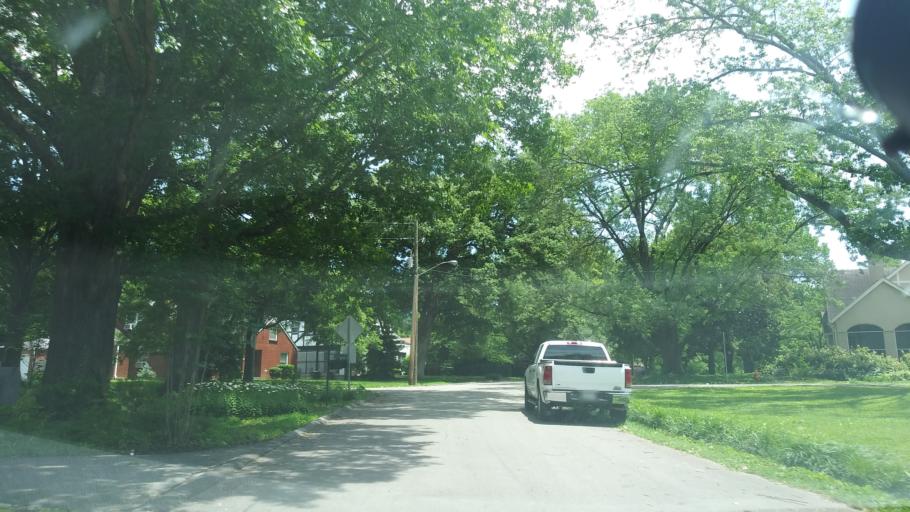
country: US
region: Tennessee
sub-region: Davidson County
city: Belle Meade
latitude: 36.1360
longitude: -86.8384
